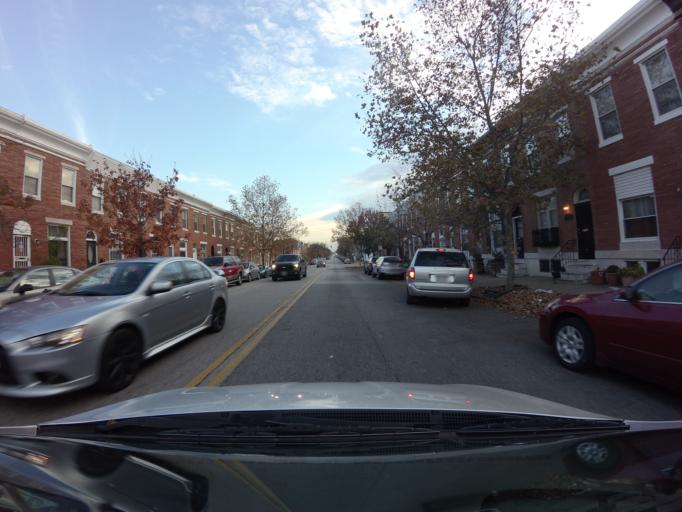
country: US
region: Maryland
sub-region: City of Baltimore
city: Baltimore
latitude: 39.2940
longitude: -76.5763
